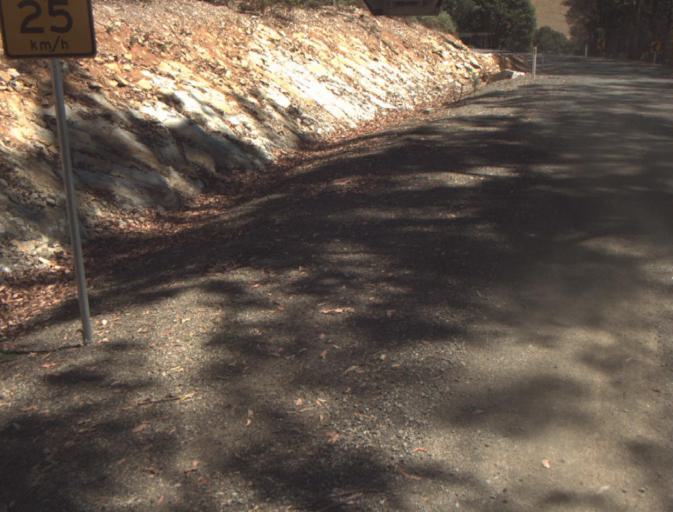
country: AU
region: Tasmania
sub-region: Dorset
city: Scottsdale
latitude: -41.2910
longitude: 147.3420
